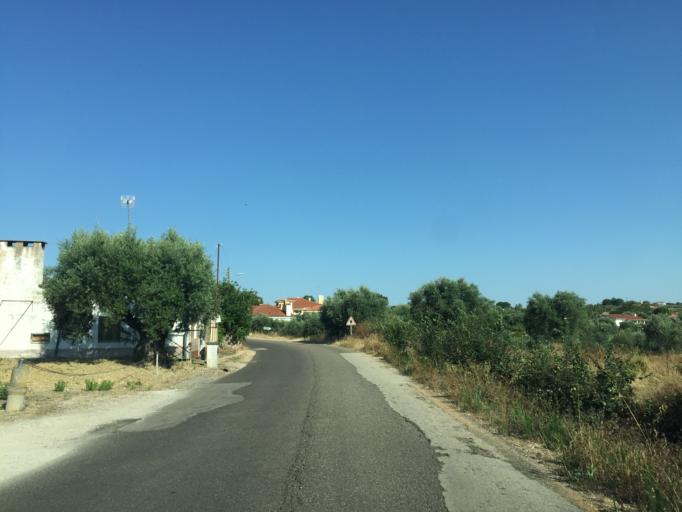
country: PT
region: Santarem
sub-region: Tomar
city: Tomar
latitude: 39.5949
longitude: -8.3700
